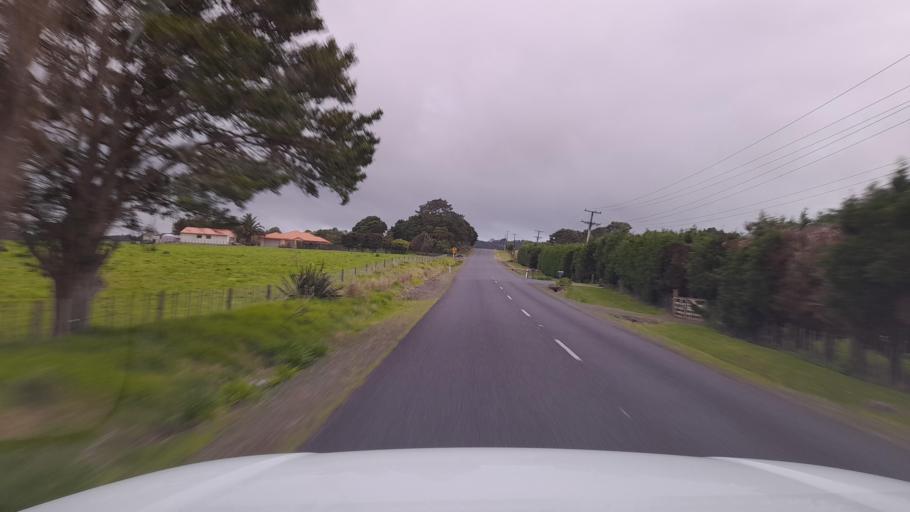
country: NZ
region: Northland
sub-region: Whangarei
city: Maungatapere
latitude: -35.6631
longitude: 174.2288
